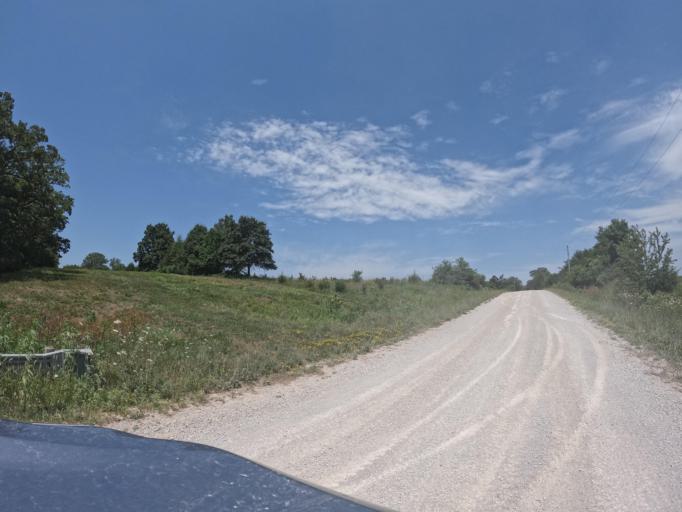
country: US
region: Iowa
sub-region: Appanoose County
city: Centerville
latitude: 40.8011
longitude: -92.9161
